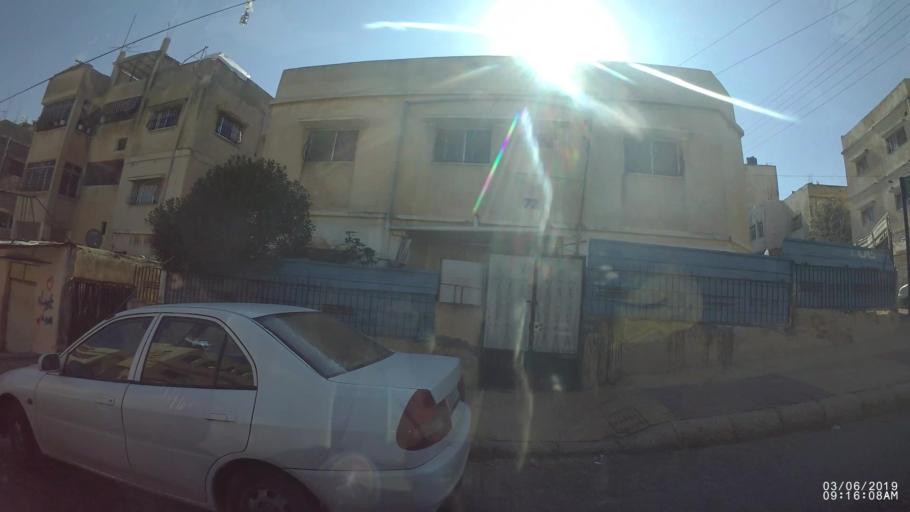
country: JO
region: Amman
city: Amman
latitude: 31.9872
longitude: 35.9883
